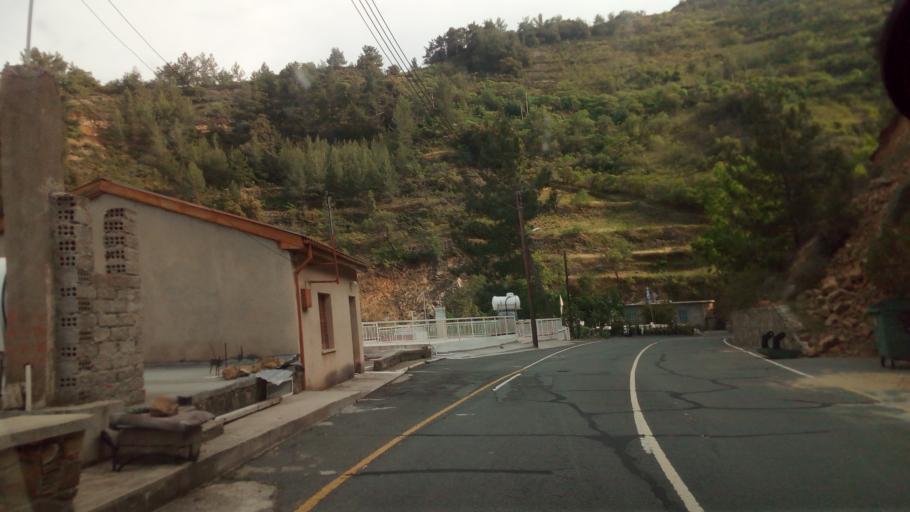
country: CY
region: Lefkosia
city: Kakopetria
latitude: 34.9984
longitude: 32.8055
